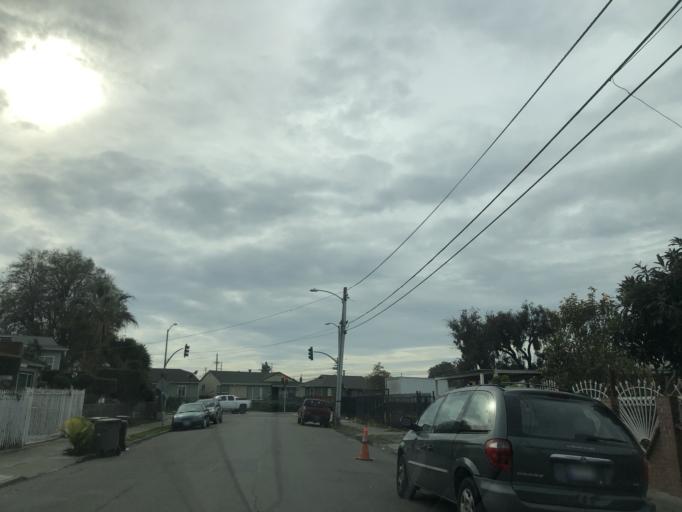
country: US
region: California
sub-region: Alameda County
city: San Leandro
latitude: 37.7378
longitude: -122.1862
